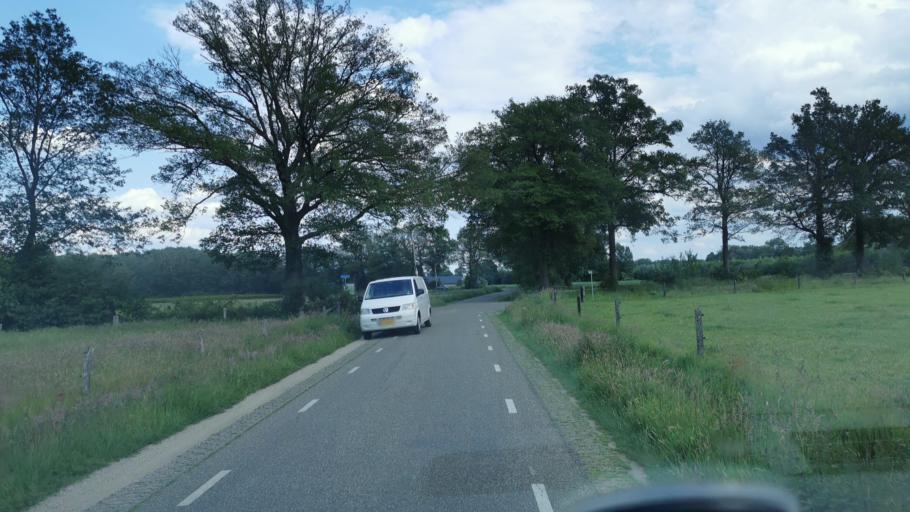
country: NL
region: Overijssel
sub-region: Gemeente Hengelo
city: Hengelo
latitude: 52.3279
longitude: 6.8276
